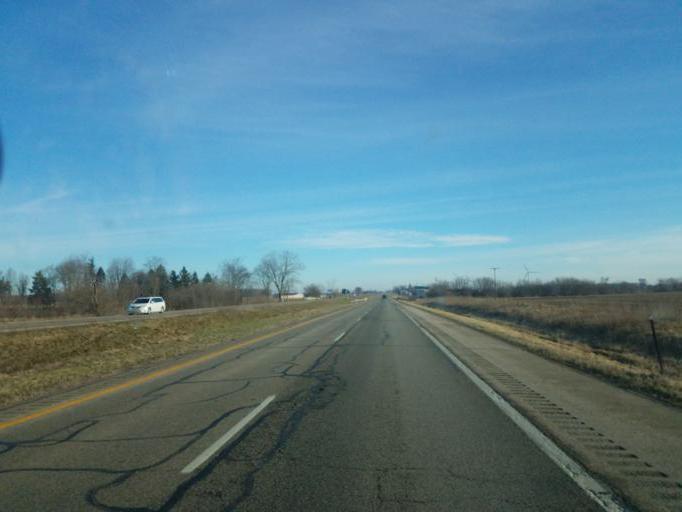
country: US
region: Michigan
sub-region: Gratiot County
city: Ithaca
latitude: 43.2425
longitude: -84.5631
